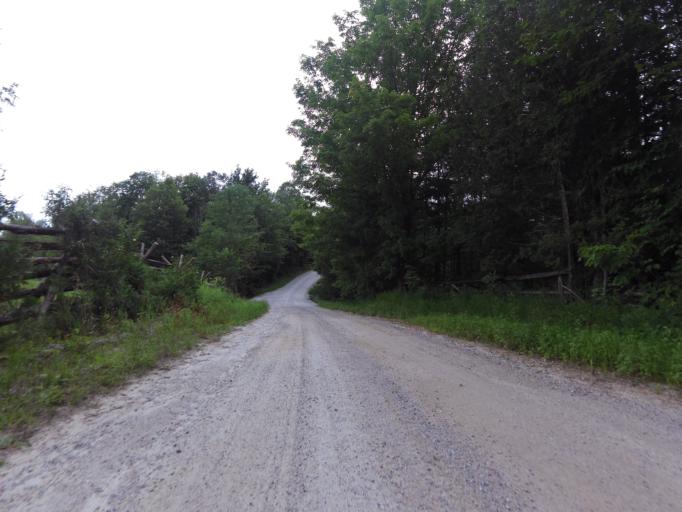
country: CA
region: Ontario
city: Perth
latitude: 44.8574
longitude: -76.5649
